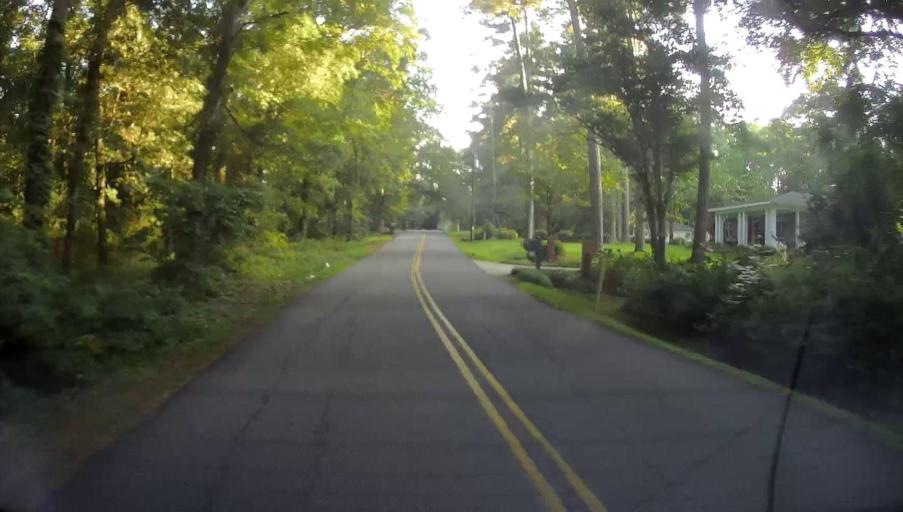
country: US
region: Georgia
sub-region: Bibb County
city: Macon
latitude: 32.8789
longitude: -83.7039
